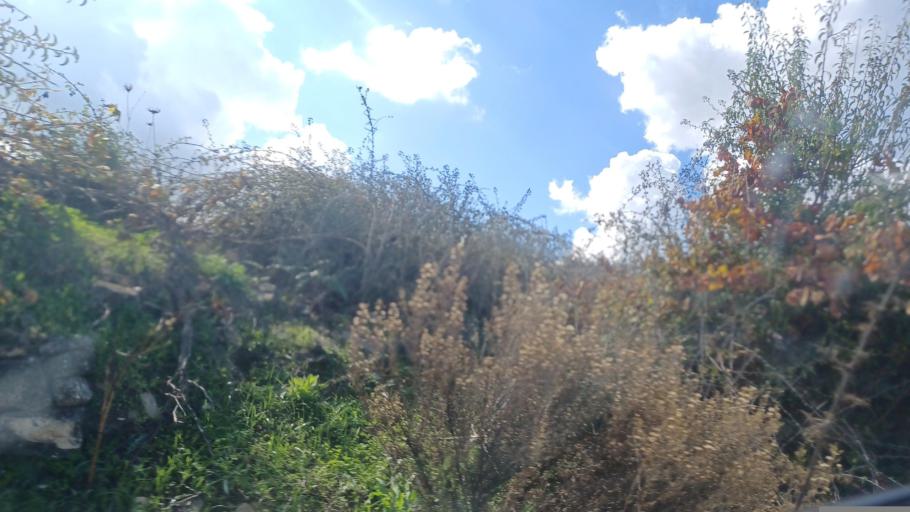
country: CY
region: Pafos
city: Mesogi
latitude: 34.8291
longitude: 32.5549
